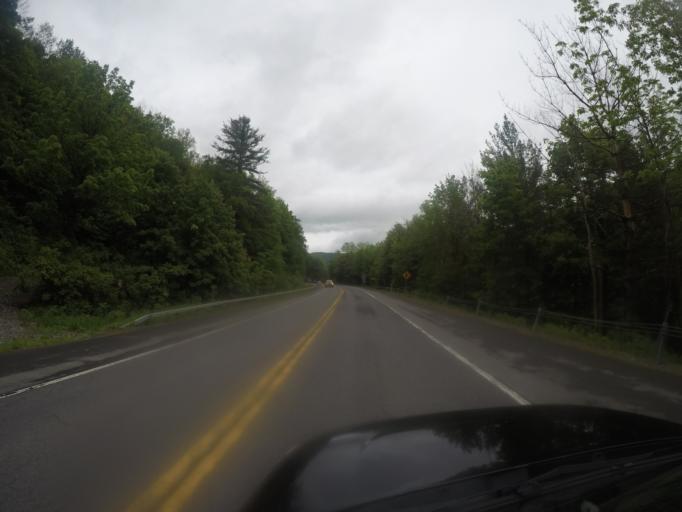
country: US
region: New York
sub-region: Ulster County
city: Shokan
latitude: 42.0780
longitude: -74.3080
